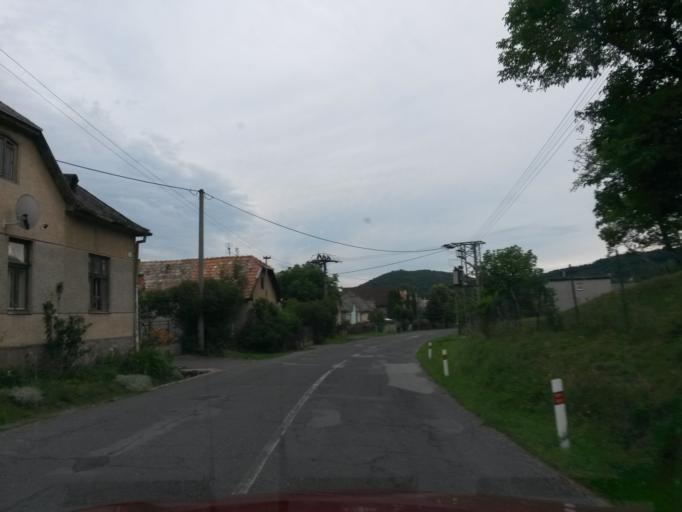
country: SK
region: Banskobystricky
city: Velky Krtis
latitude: 48.3095
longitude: 19.3959
